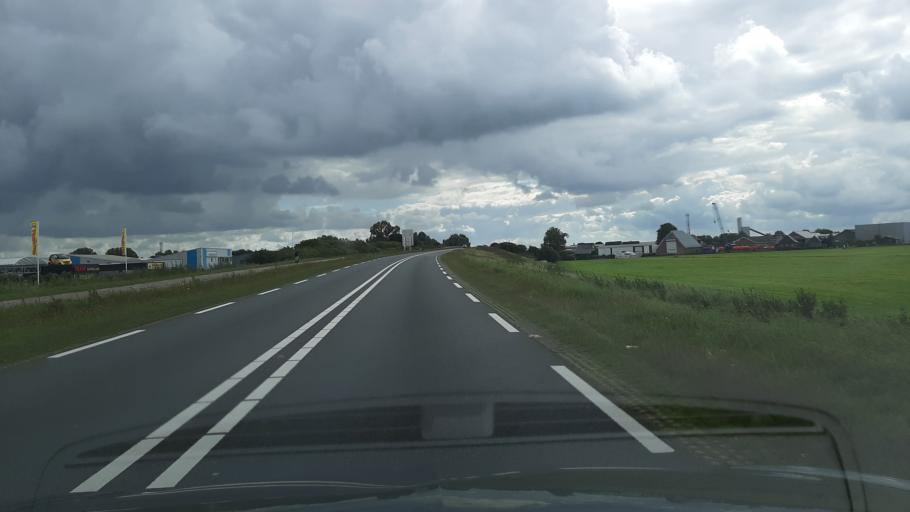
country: NL
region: Overijssel
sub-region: Gemeente Steenwijkerland
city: Tuk
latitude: 52.7881
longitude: 6.0914
